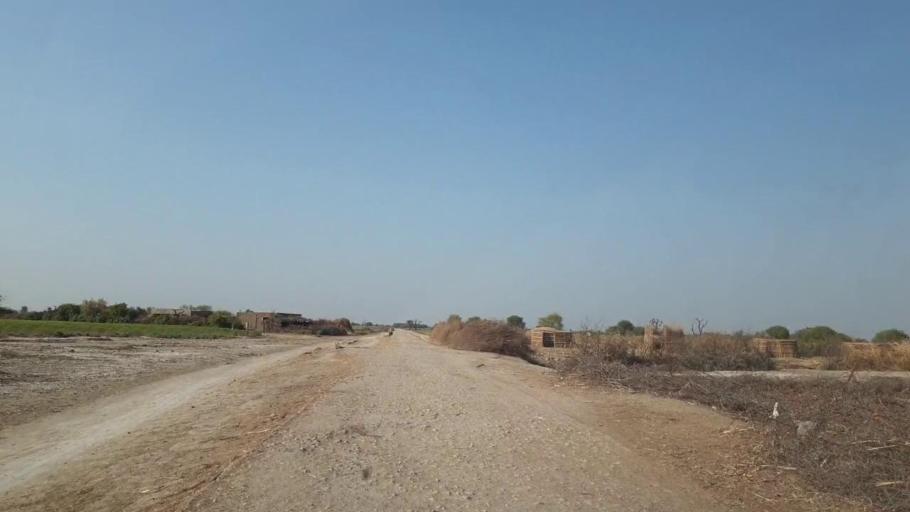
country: PK
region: Sindh
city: Tando Mittha Khan
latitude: 25.7539
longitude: 69.1972
